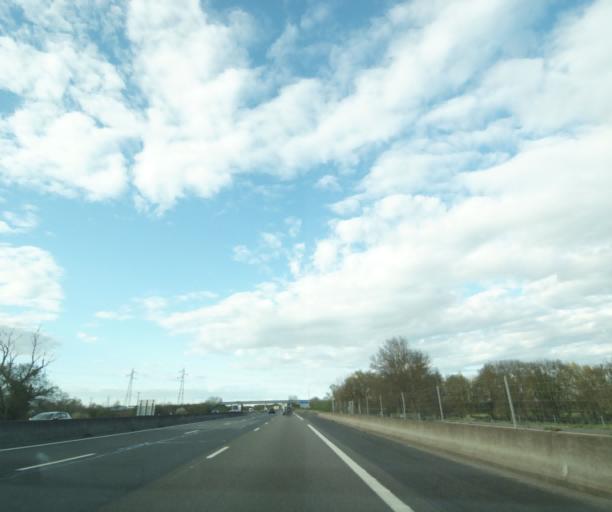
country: FR
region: Bourgogne
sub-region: Departement de Saone-et-Loire
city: Creches-sur-Saone
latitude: 46.2402
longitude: 4.7976
